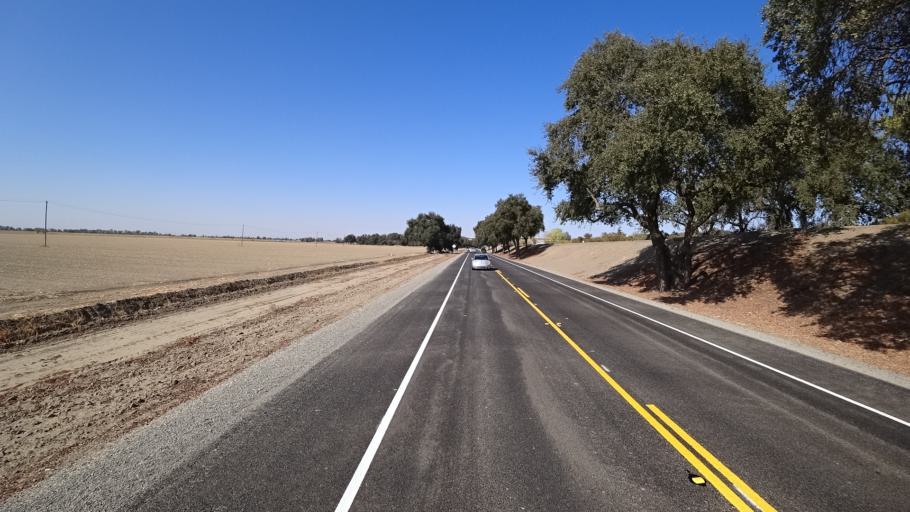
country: US
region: California
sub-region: Yolo County
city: West Sacramento
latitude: 38.6679
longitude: -121.6218
